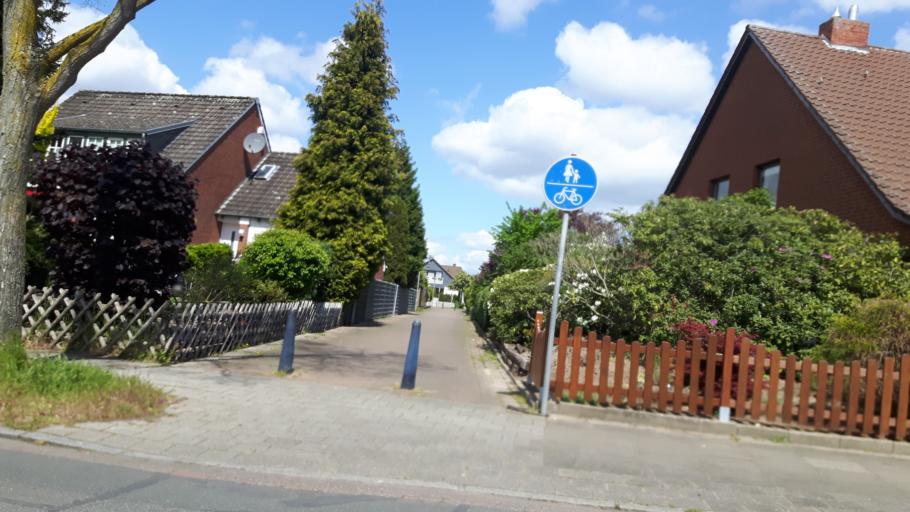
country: DE
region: Bremen
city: Bremen
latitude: 53.0453
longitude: 8.8542
